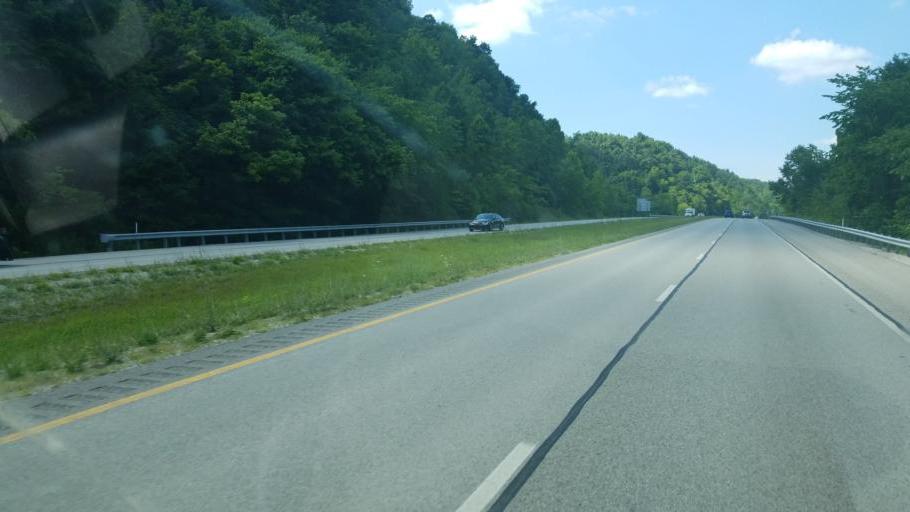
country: US
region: West Virginia
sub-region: Kanawha County
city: Sissonville
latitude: 38.6245
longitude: -81.6454
